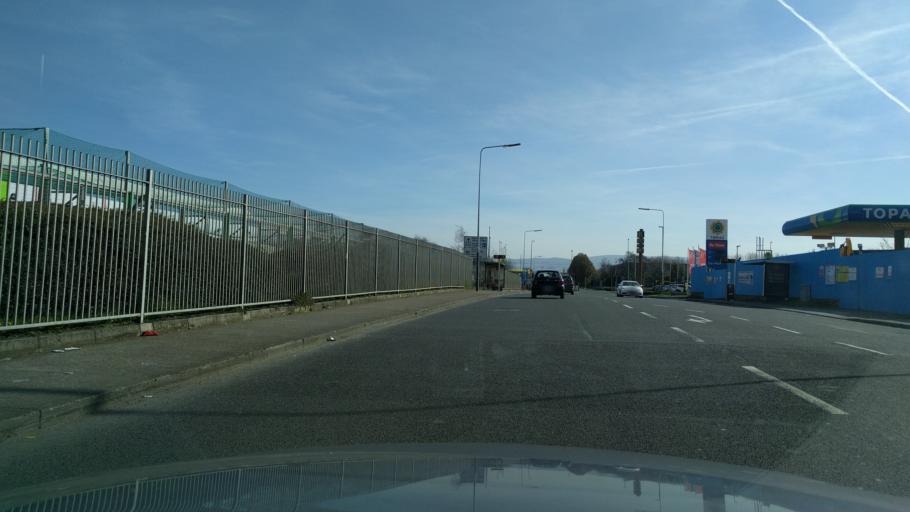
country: IE
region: Leinster
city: Crumlin
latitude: 53.3284
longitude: -6.3438
